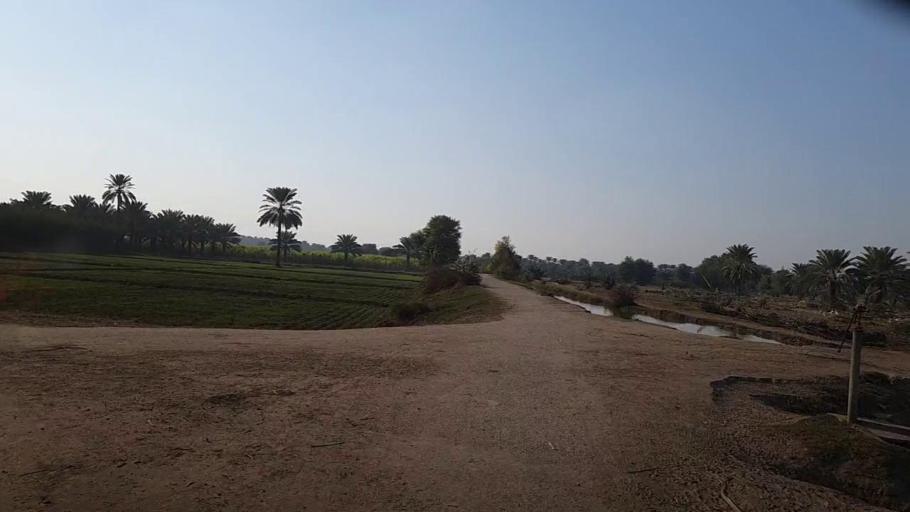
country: PK
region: Sindh
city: Ranipur
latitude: 27.2515
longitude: 68.5523
